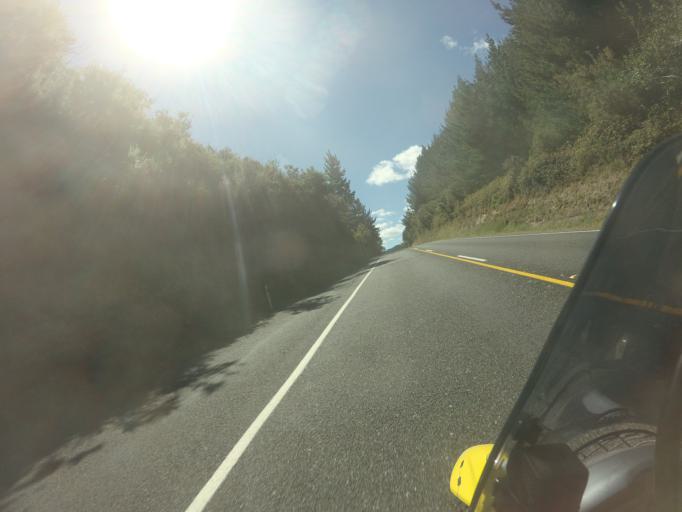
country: NZ
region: Bay of Plenty
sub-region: Whakatane District
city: Murupara
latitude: -38.3086
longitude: 176.8095
